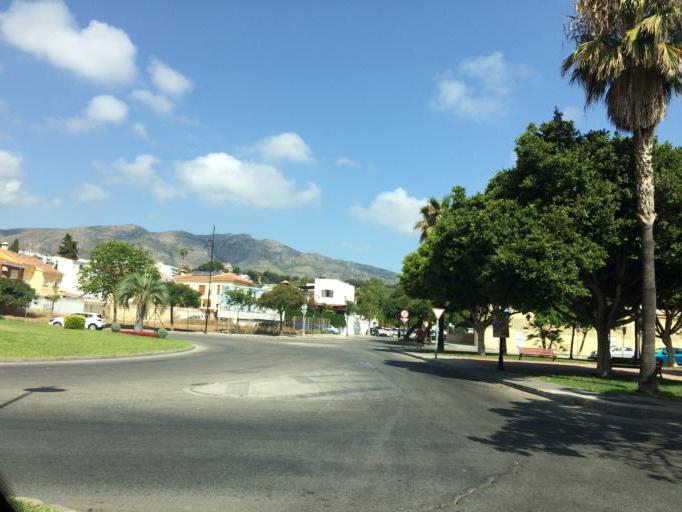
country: ES
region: Andalusia
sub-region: Provincia de Malaga
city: Torremolinos
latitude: 36.6331
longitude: -4.4913
